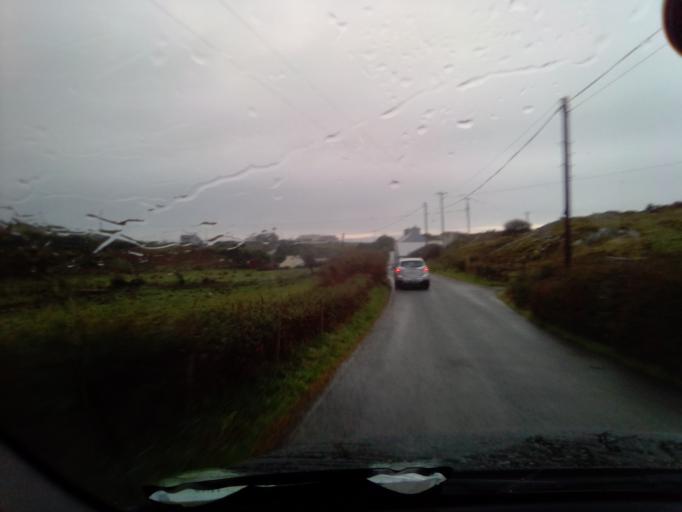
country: IE
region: Ulster
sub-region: County Donegal
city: Ramelton
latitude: 55.2681
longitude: -7.6544
